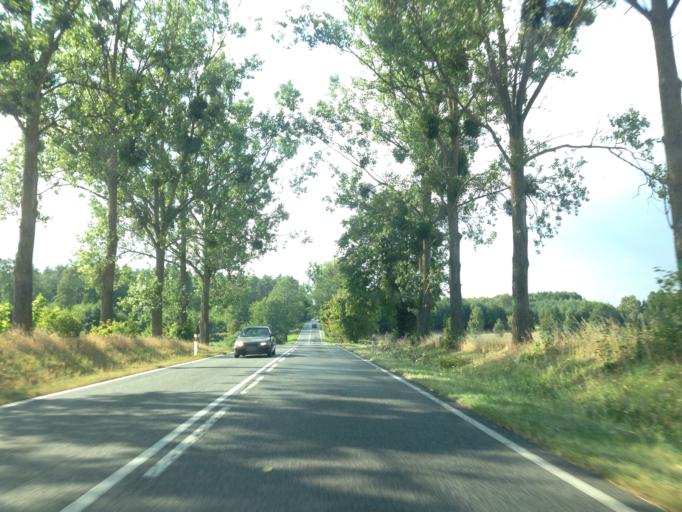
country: PL
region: Kujawsko-Pomorskie
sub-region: Powiat swiecki
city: Bukowiec
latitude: 53.4643
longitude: 18.1786
